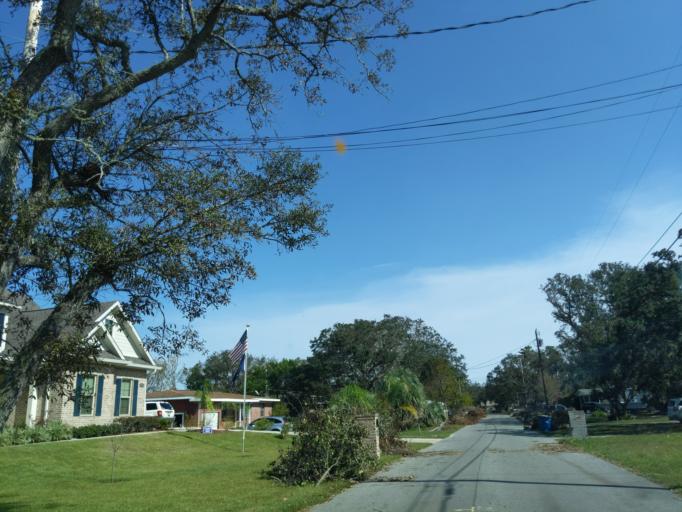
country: US
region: Florida
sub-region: Santa Rosa County
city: Gulf Breeze
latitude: 30.3549
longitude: -87.1896
